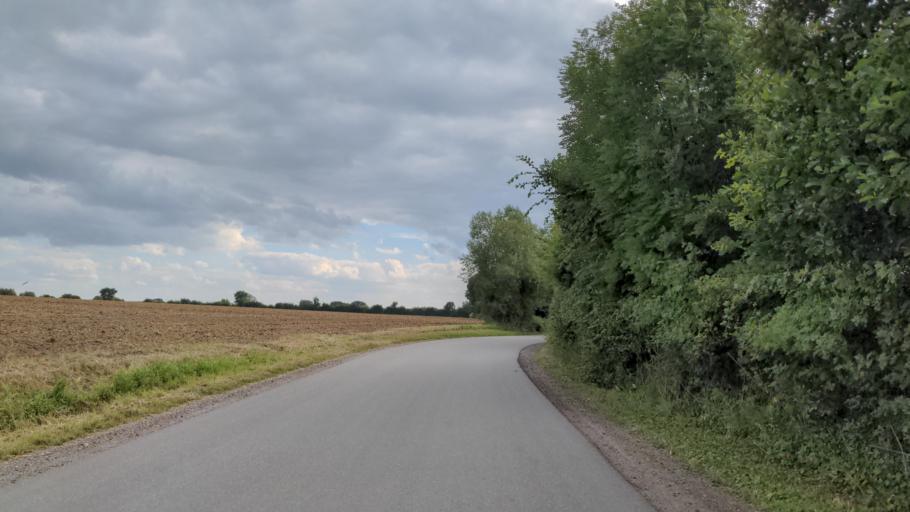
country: DE
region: Schleswig-Holstein
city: Dahme
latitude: 54.2097
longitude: 11.0818
